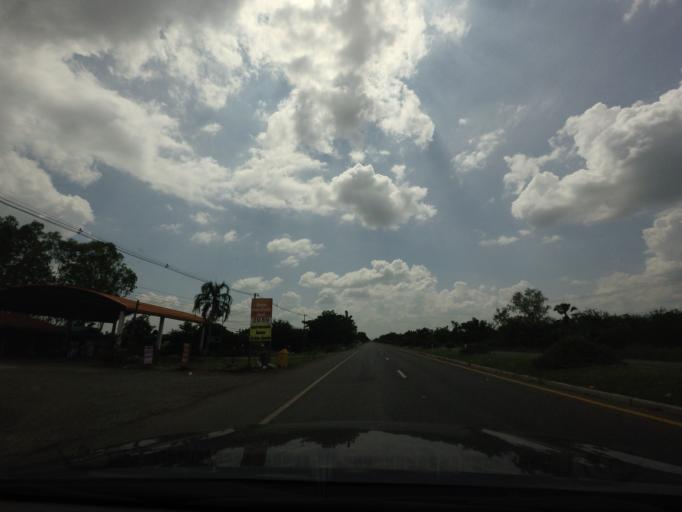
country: TH
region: Phetchabun
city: Nong Phai
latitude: 16.1731
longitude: 101.0797
